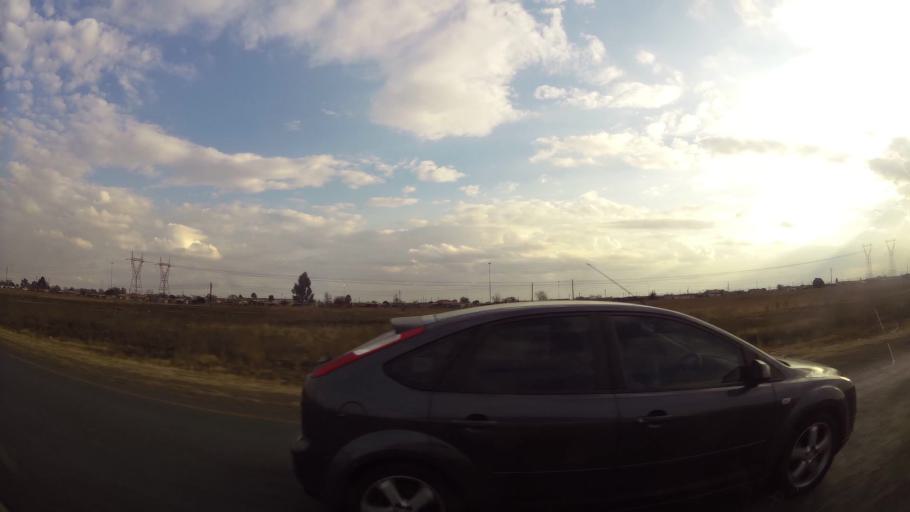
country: ZA
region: Gauteng
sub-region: Sedibeng District Municipality
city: Vanderbijlpark
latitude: -26.6859
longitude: 27.7998
